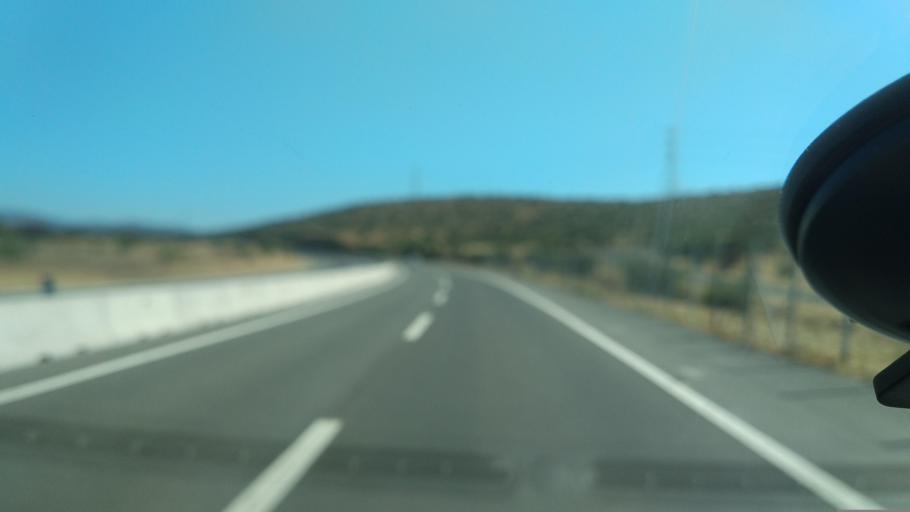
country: CL
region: Valparaiso
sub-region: Provincia de Marga Marga
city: Villa Alemana
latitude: -32.9939
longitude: -71.3294
